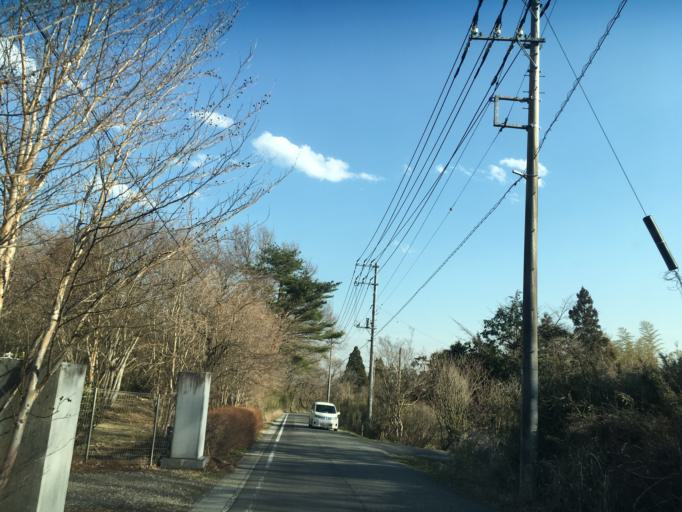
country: JP
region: Tochigi
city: Kuroiso
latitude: 37.0617
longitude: 140.0052
